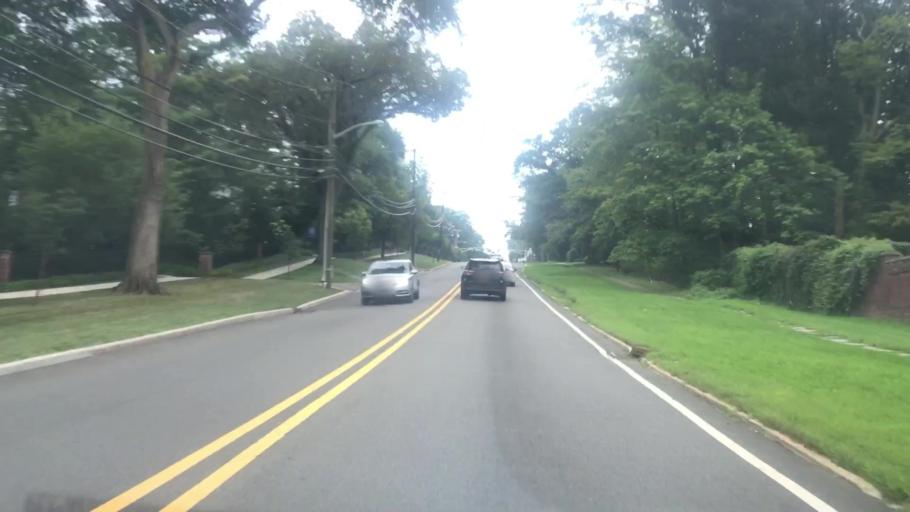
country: US
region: New Jersey
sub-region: Bergen County
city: Englewood
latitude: 40.8877
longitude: -73.9639
